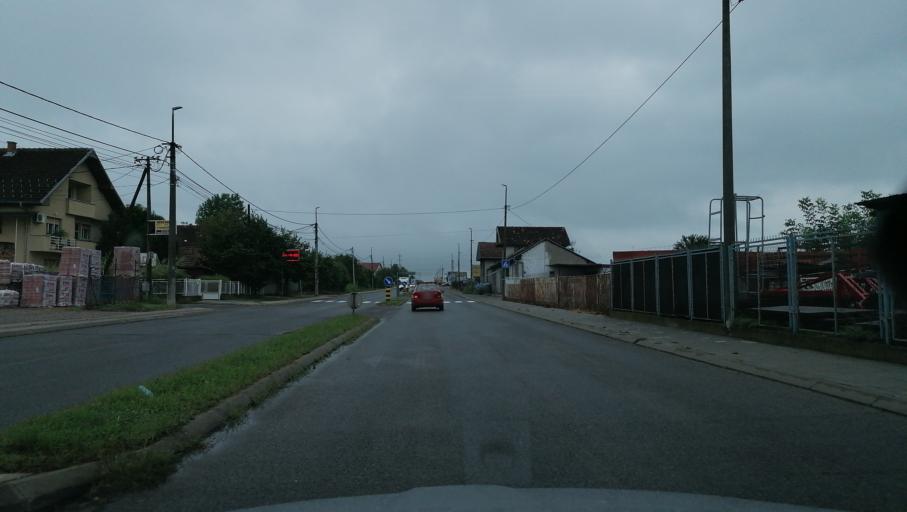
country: RS
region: Central Serbia
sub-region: Rasinski Okrug
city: Krusevac
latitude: 43.5864
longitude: 21.2906
